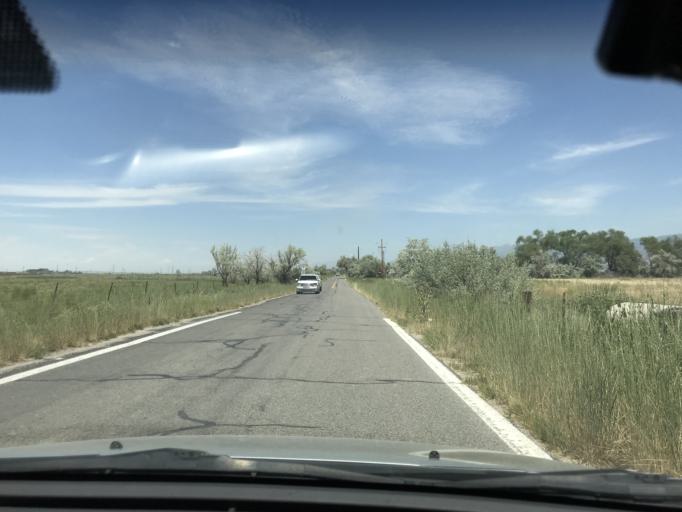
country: US
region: Utah
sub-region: Davis County
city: North Salt Lake
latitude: 40.8189
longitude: -111.9535
